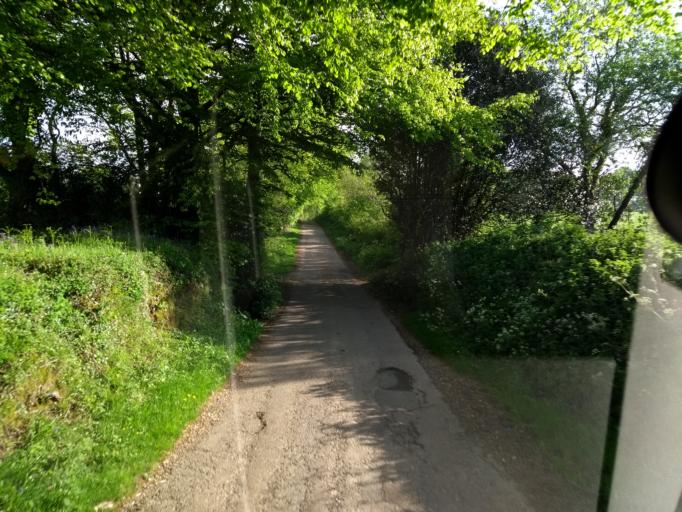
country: GB
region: England
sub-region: Dorset
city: Lyme Regis
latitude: 50.7901
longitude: -2.9296
